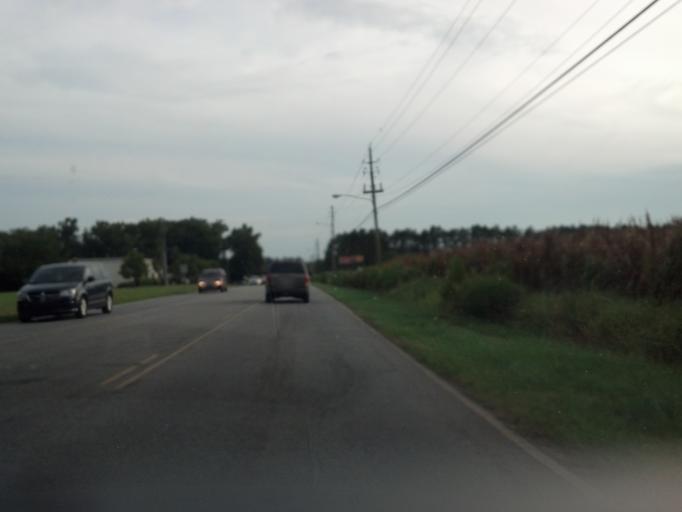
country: US
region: North Carolina
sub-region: Pitt County
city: Summerfield
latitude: 35.5653
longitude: -77.3844
